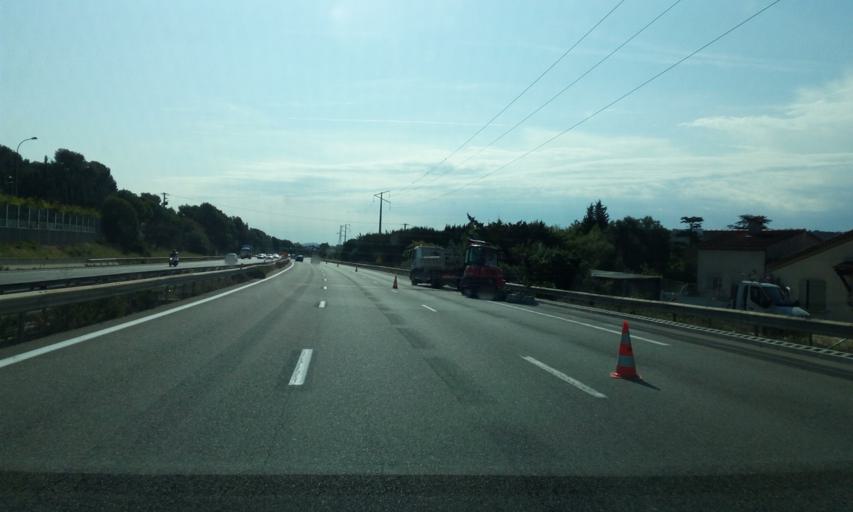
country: FR
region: Provence-Alpes-Cote d'Azur
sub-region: Departement du Var
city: Sanary-sur-Mer
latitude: 43.1288
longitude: 5.8180
